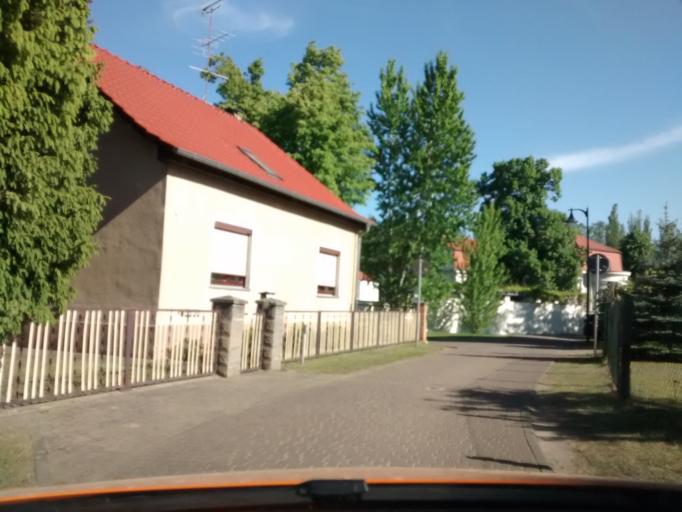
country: DE
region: Brandenburg
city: Bad Saarow
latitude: 52.2658
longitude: 14.0668
